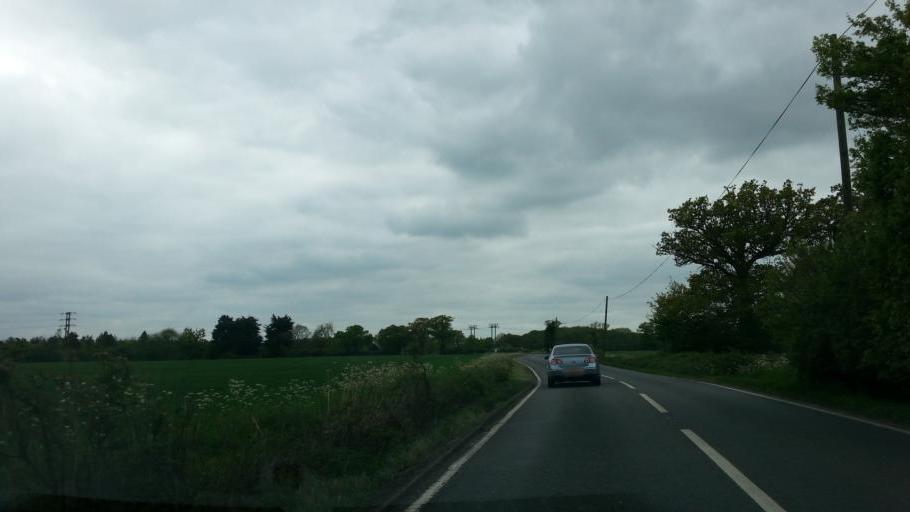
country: GB
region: England
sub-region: Suffolk
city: Capel Saint Mary
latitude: 52.0560
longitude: 1.0146
